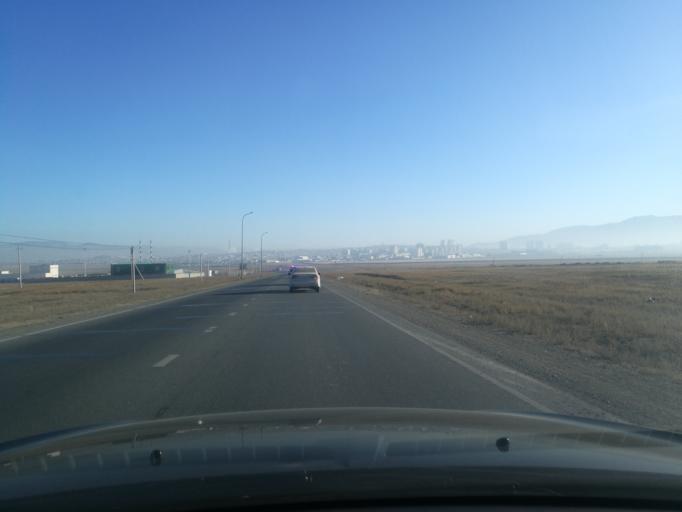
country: MN
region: Ulaanbaatar
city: Ulaanbaatar
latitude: 47.8479
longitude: 106.7359
